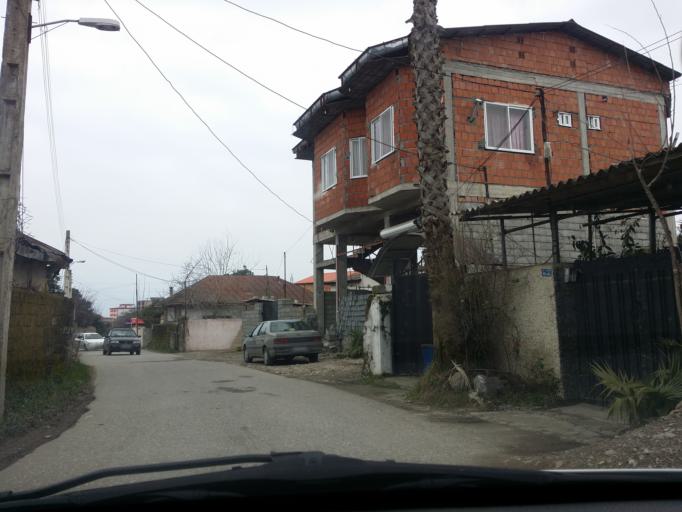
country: IR
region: Mazandaran
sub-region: Nowshahr
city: Nowshahr
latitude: 36.6465
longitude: 51.4792
